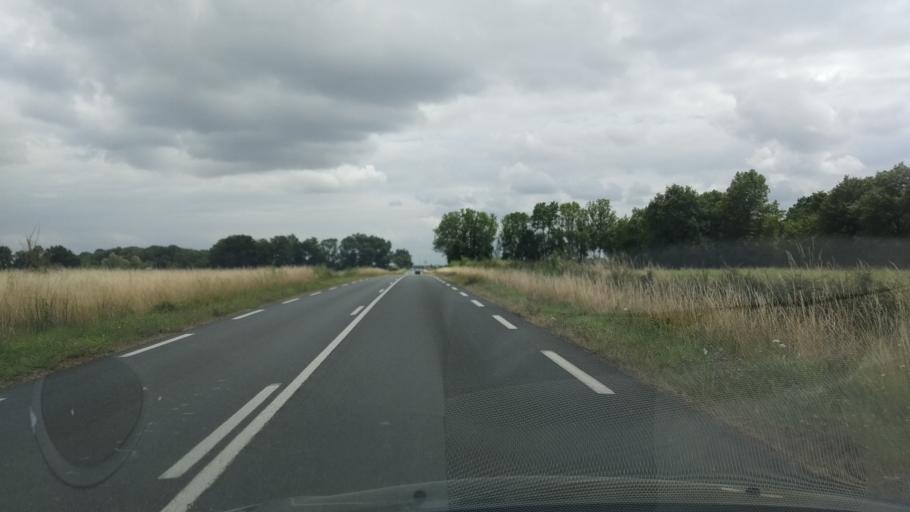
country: FR
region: Poitou-Charentes
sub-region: Departement de la Vienne
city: Saint-Maurice-la-Clouere
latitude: 46.3941
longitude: 0.3985
